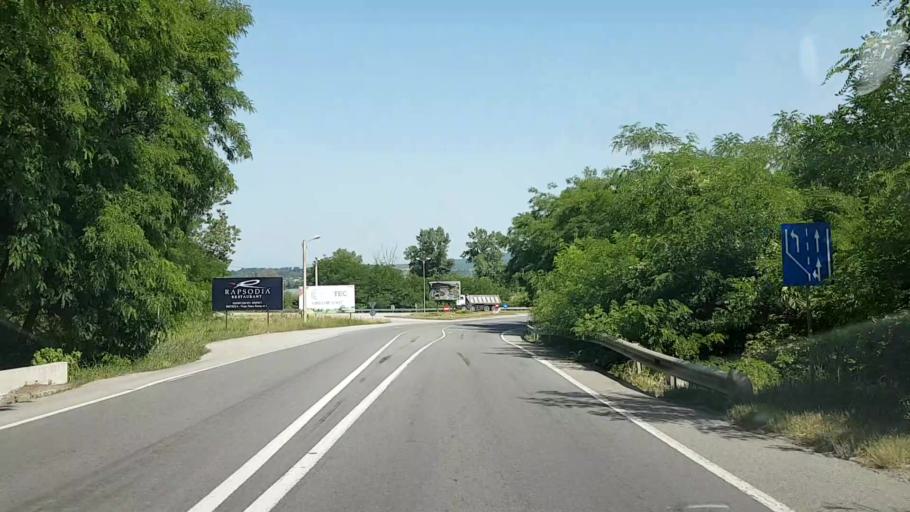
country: RO
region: Bistrita-Nasaud
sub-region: Comuna Beclean
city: Beclean
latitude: 47.1788
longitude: 24.1455
